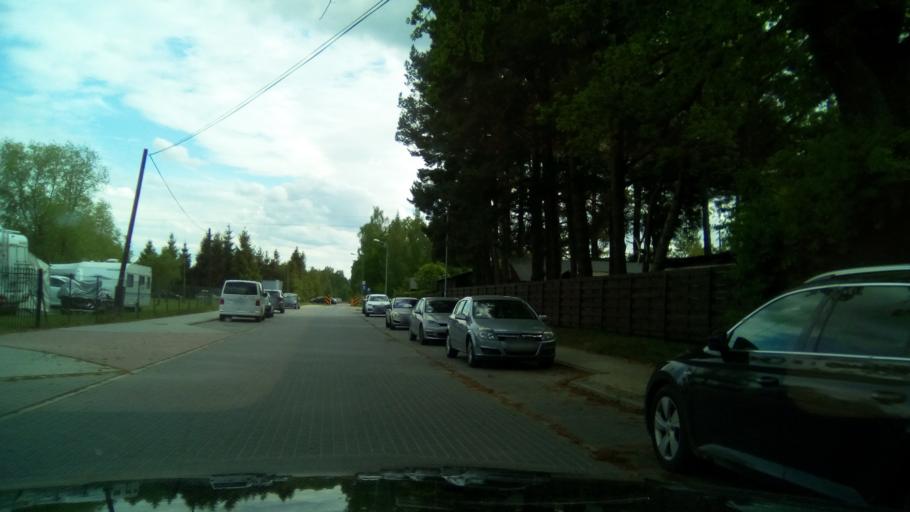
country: PL
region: Pomeranian Voivodeship
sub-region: Powiat pucki
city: Wierzchucino
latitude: 54.8282
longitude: 18.0764
